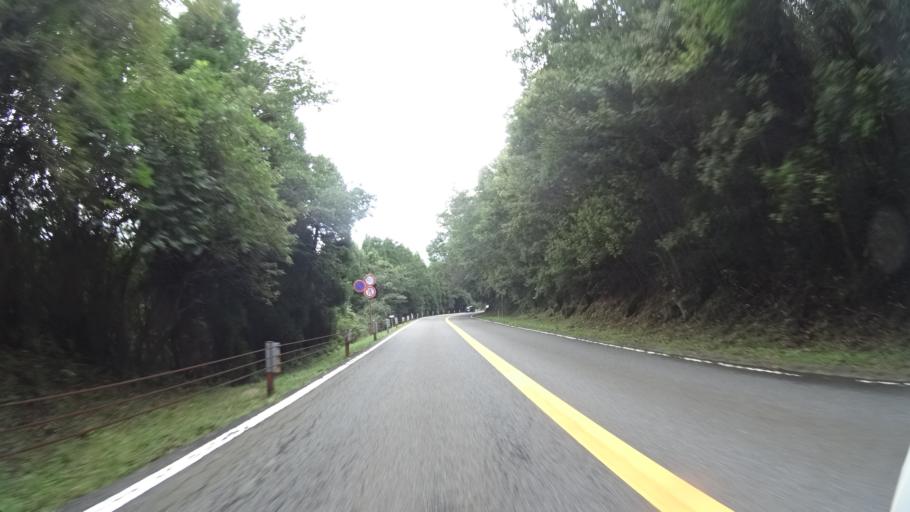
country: JP
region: Oita
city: Tsukawaki
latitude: 33.1069
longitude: 131.2197
